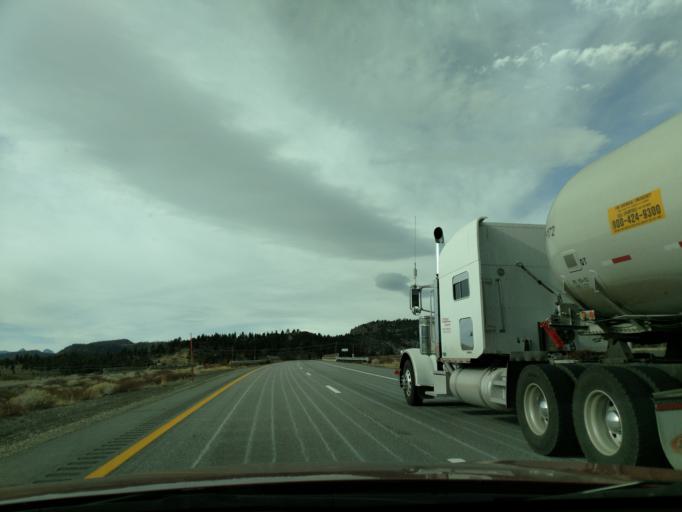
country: US
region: California
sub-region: Mono County
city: Mammoth Lakes
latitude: 37.6407
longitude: -118.9153
